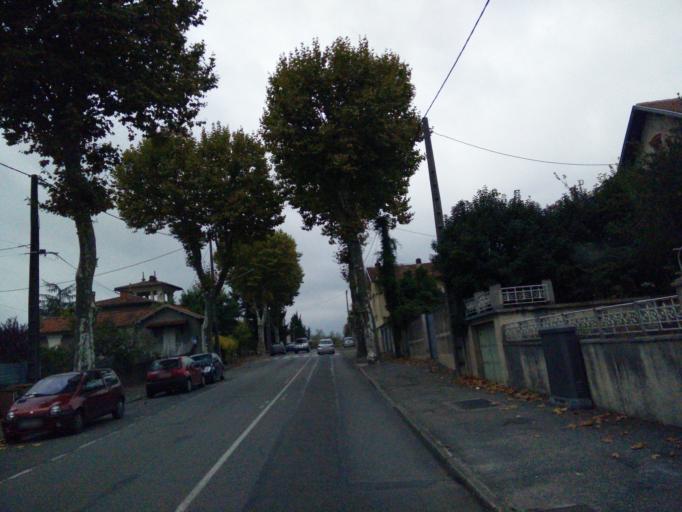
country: FR
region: Midi-Pyrenees
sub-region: Departement du Lot
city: Cahors
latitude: 44.4575
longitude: 1.4348
